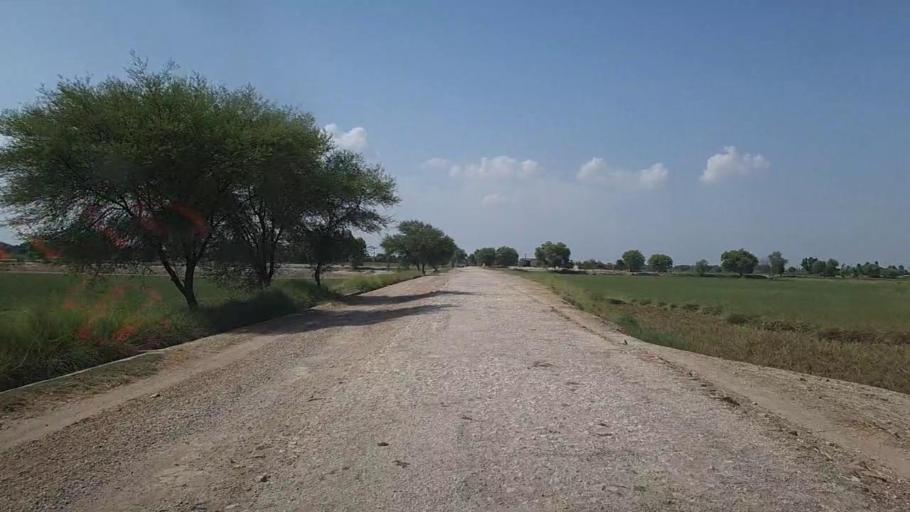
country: PK
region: Sindh
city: Khairpur
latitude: 28.1104
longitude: 69.6207
